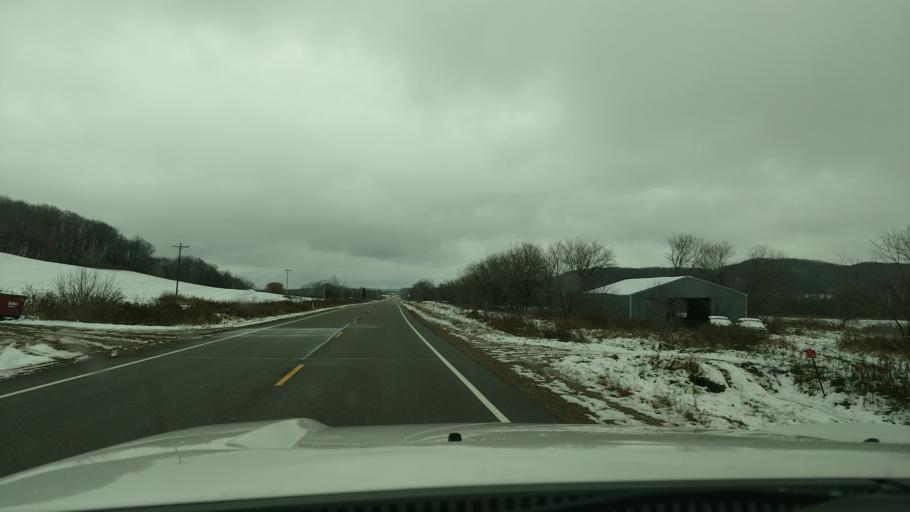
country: US
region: Wisconsin
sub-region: Dunn County
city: Colfax
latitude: 45.1370
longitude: -91.7960
